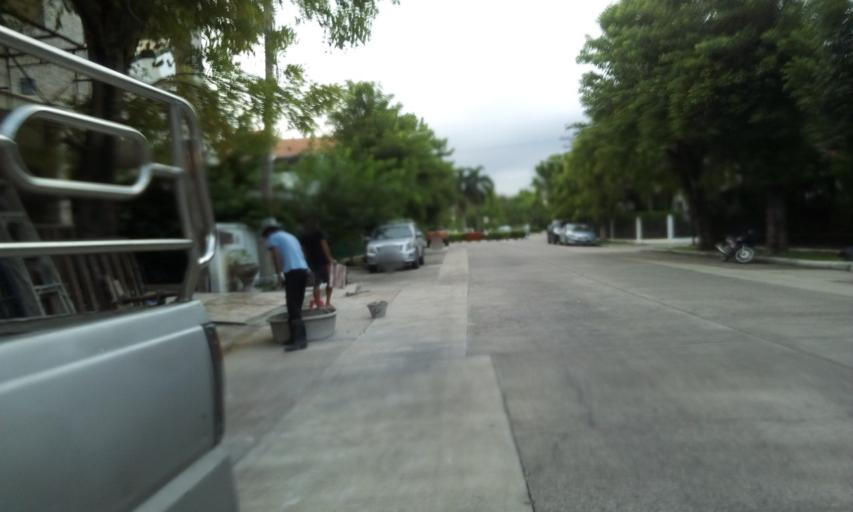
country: TH
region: Pathum Thani
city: Ban Rangsit
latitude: 14.0499
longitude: 100.8288
